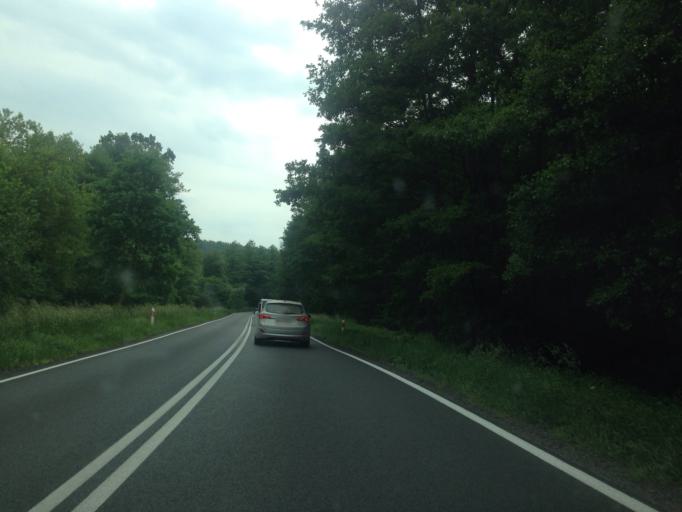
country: PL
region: Kujawsko-Pomorskie
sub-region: Powiat grudziadzki
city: Rogozno
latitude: 53.5086
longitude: 18.9256
